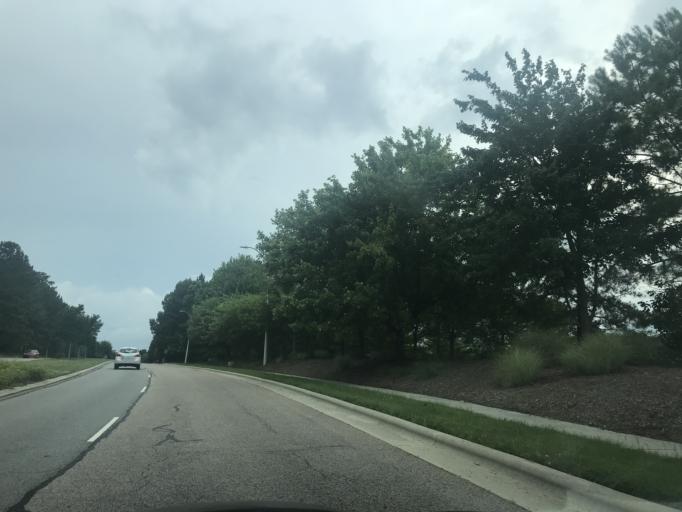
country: US
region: North Carolina
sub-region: Wake County
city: Morrisville
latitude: 35.8151
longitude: -78.8532
